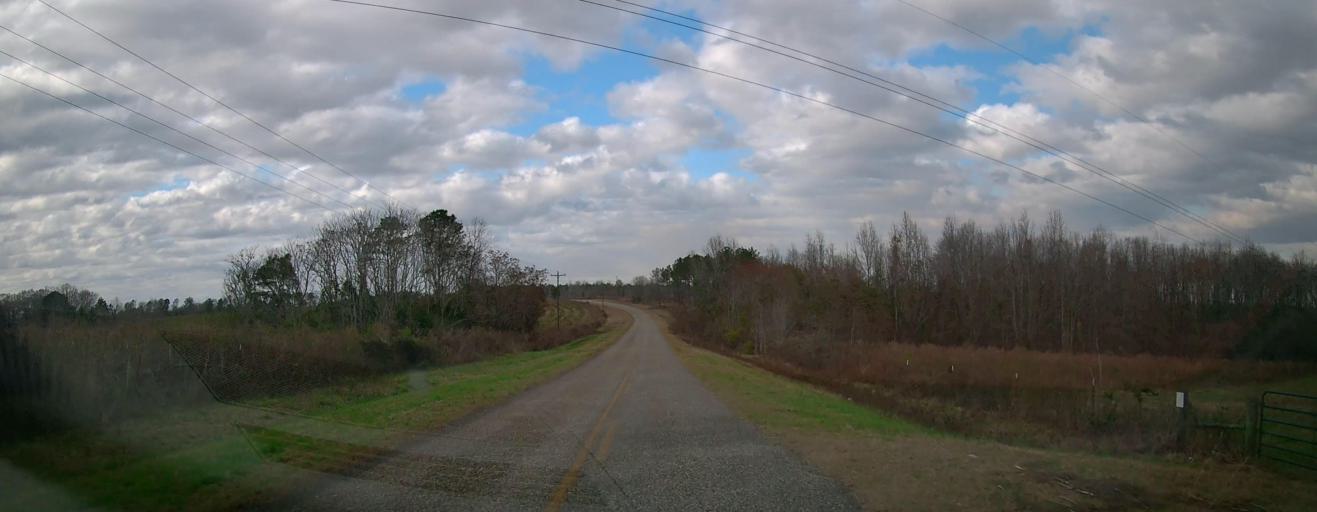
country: US
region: Georgia
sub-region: Marion County
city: Buena Vista
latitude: 32.4143
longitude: -84.4111
